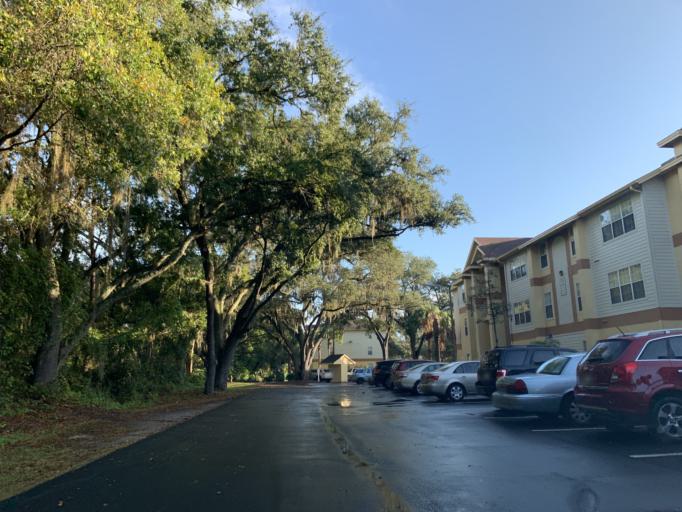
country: US
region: Florida
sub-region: Hillsborough County
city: Mango
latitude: 27.9773
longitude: -82.3203
